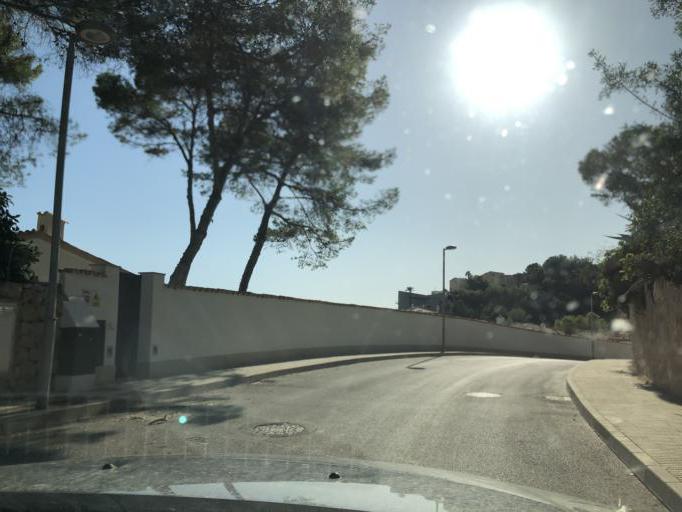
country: ES
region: Balearic Islands
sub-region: Illes Balears
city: Camp de Mar
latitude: 39.5397
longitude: 2.4136
